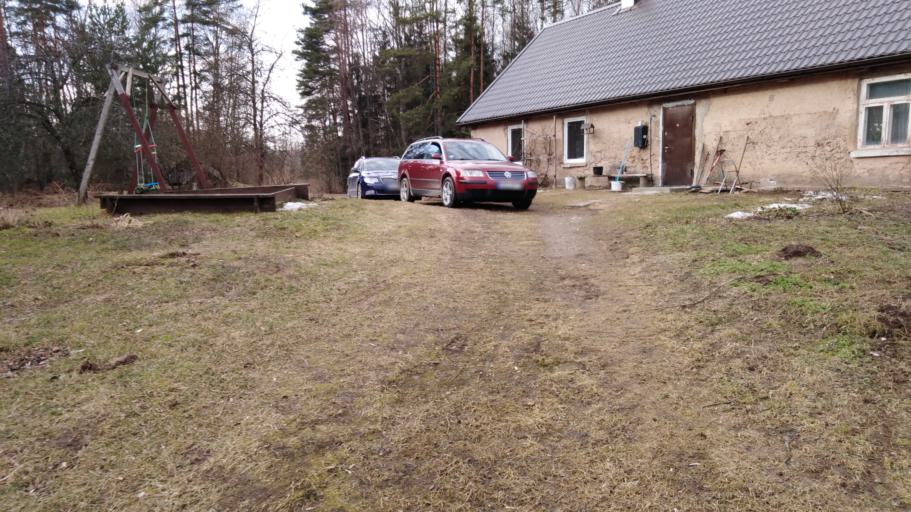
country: LV
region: Kuldigas Rajons
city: Kuldiga
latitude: 57.0361
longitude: 21.8555
